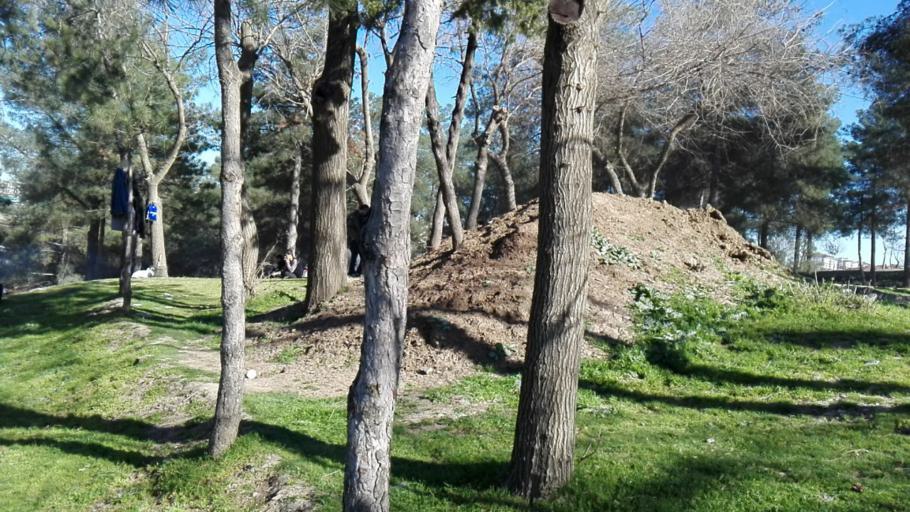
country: TR
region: Batman
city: Demiryol
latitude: 37.9088
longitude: 41.1313
